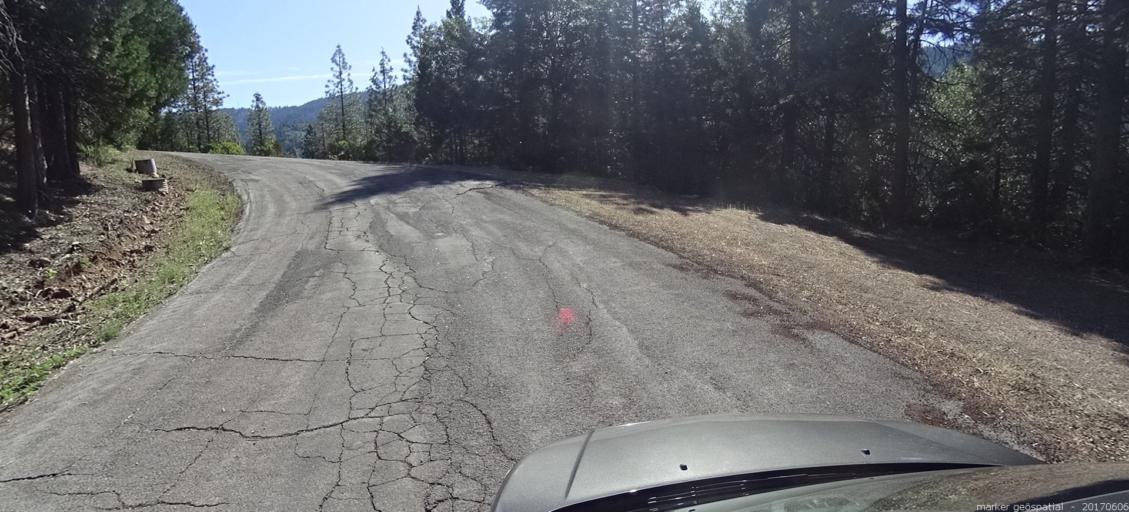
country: US
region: California
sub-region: Siskiyou County
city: Dunsmuir
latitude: 41.2005
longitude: -122.2795
